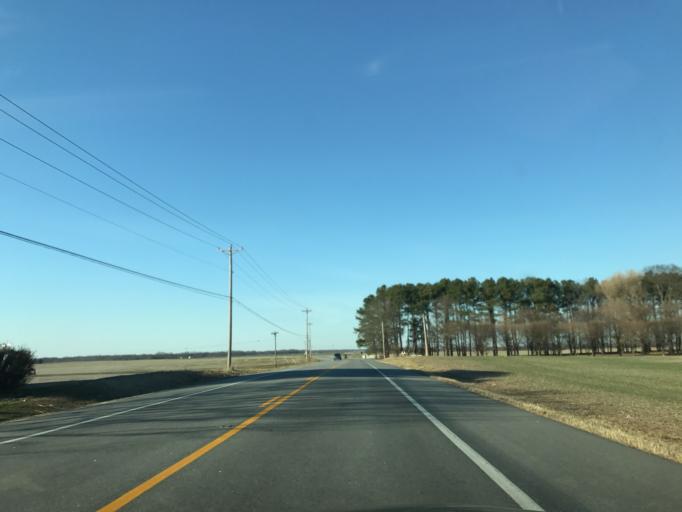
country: US
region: Maryland
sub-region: Queen Anne's County
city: Kingstown
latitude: 39.2011
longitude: -75.8627
